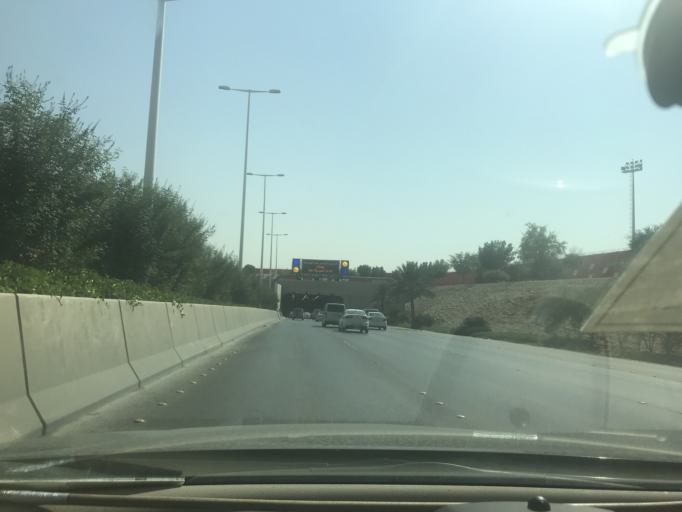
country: SA
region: Ar Riyad
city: Riyadh
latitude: 24.7123
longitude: 46.7191
